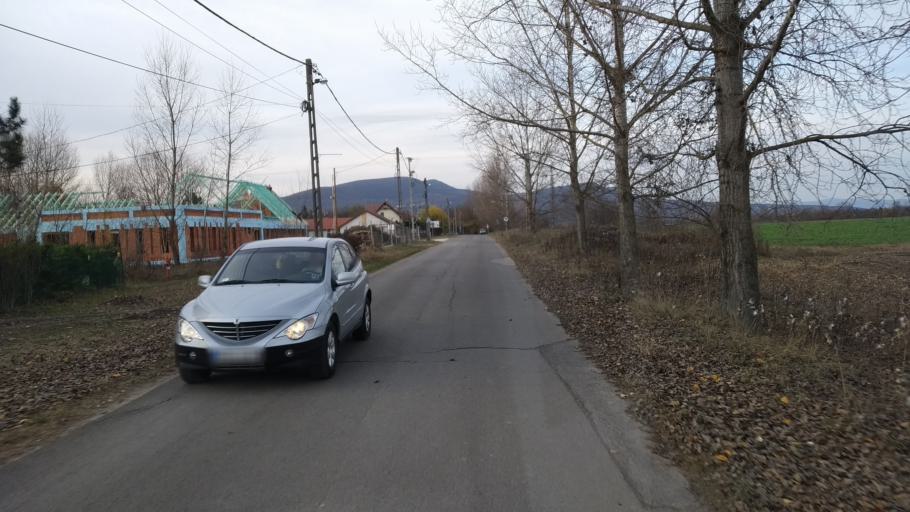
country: HU
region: Pest
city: God
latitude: 47.6857
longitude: 19.1141
